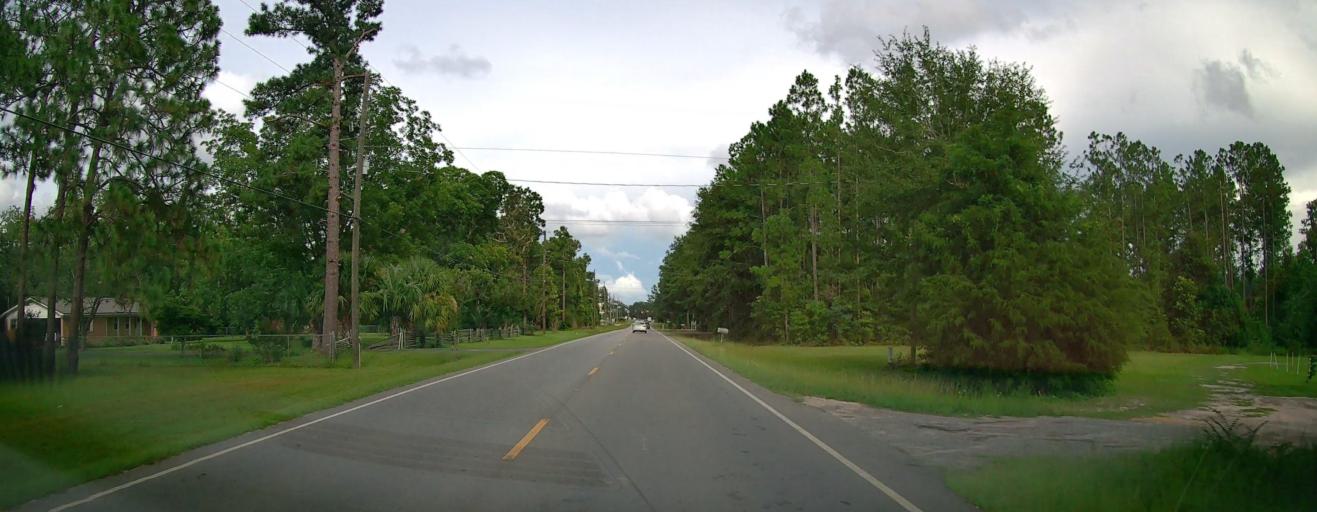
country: US
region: Georgia
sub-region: Wayne County
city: Jesup
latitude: 31.6624
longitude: -81.8540
